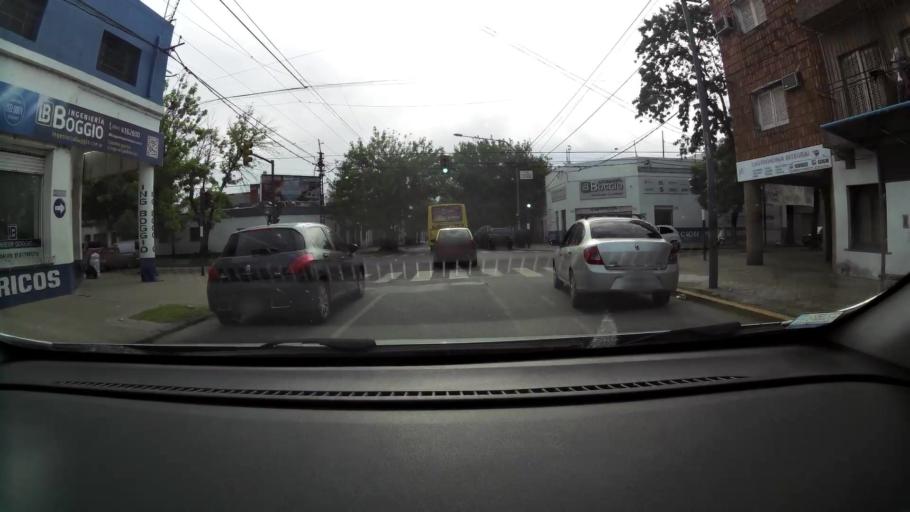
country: AR
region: Santa Fe
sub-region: Departamento de Rosario
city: Rosario
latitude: -32.9249
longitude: -60.6734
